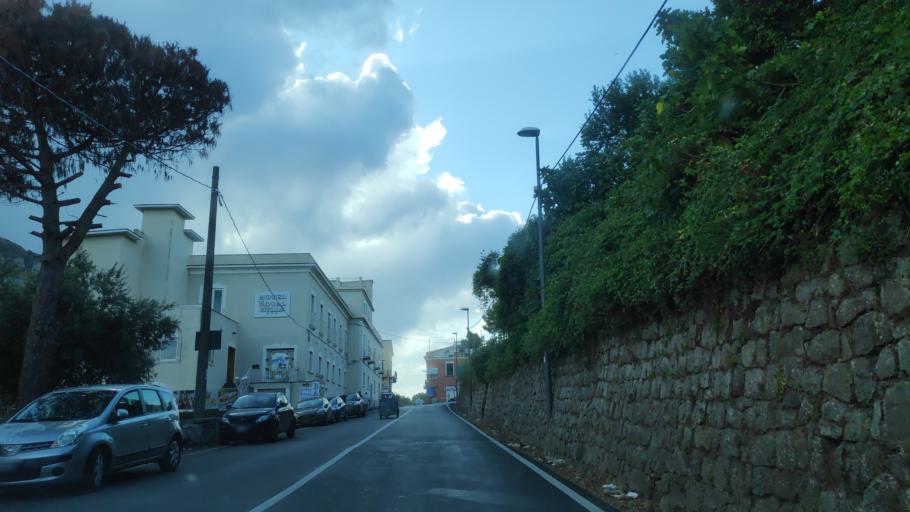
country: IT
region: Campania
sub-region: Provincia di Napoli
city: Piano di Sorrento
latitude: 40.6179
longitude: 14.4265
